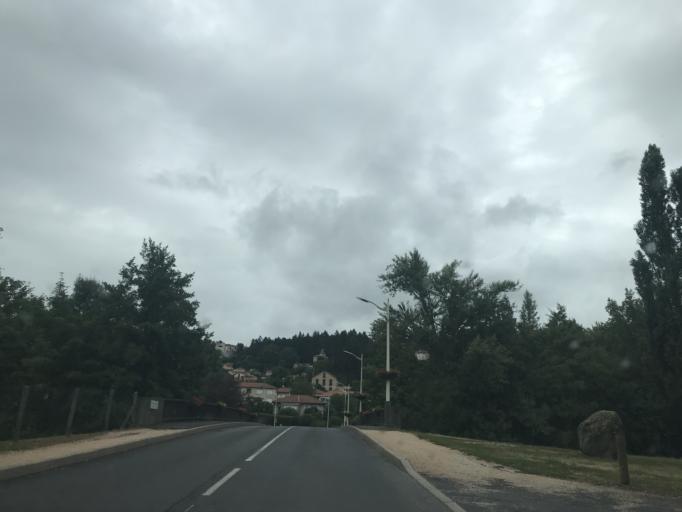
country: FR
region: Auvergne
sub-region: Departement de la Haute-Loire
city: Le Puy-en-Velay
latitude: 45.0512
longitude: 3.8819
